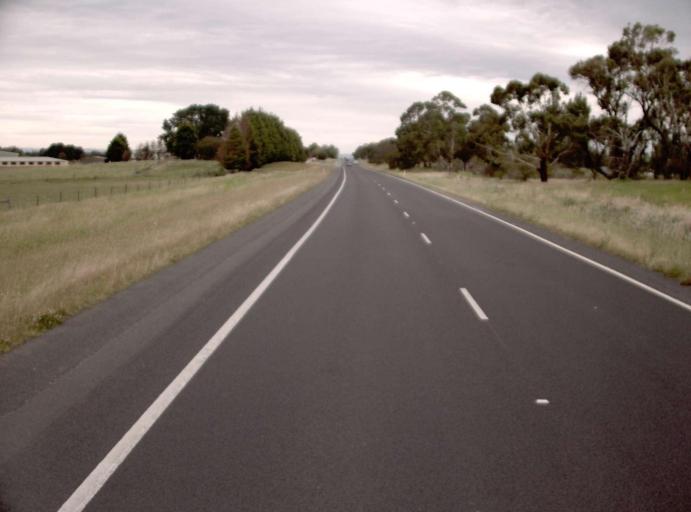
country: AU
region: Victoria
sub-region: Casey
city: Junction Village
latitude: -38.1379
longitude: 145.3027
